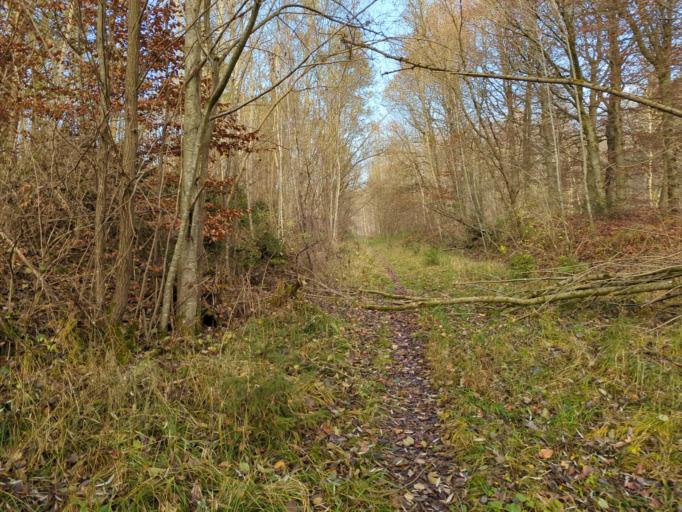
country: DE
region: Bavaria
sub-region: Swabia
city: Wasserburg
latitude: 48.4206
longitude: 10.3018
